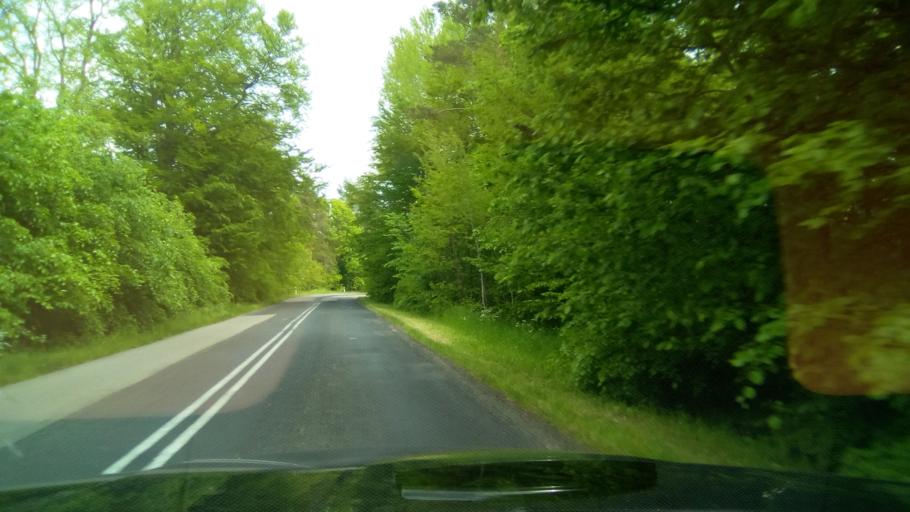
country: PL
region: Pomeranian Voivodeship
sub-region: Powiat leborski
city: Cewice
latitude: 54.3842
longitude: 17.6619
